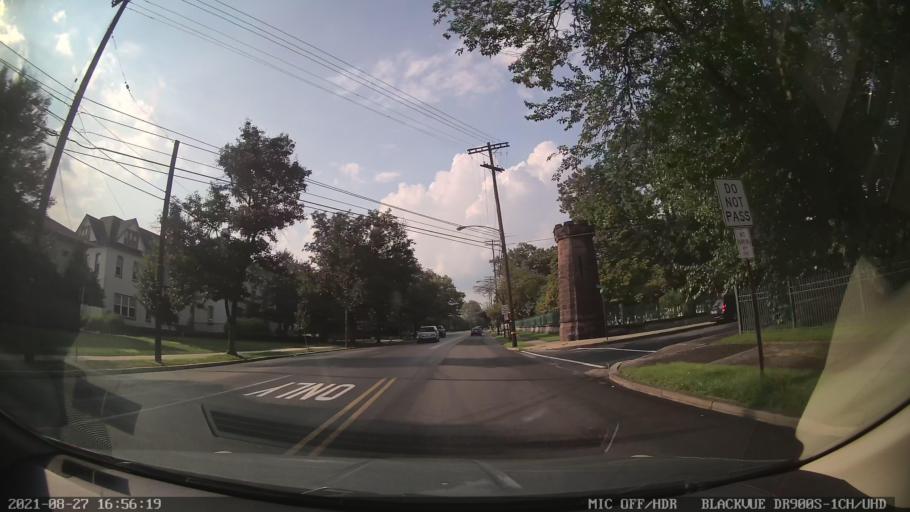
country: US
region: Pennsylvania
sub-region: Berks County
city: Reading
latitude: 40.3507
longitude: -75.9327
